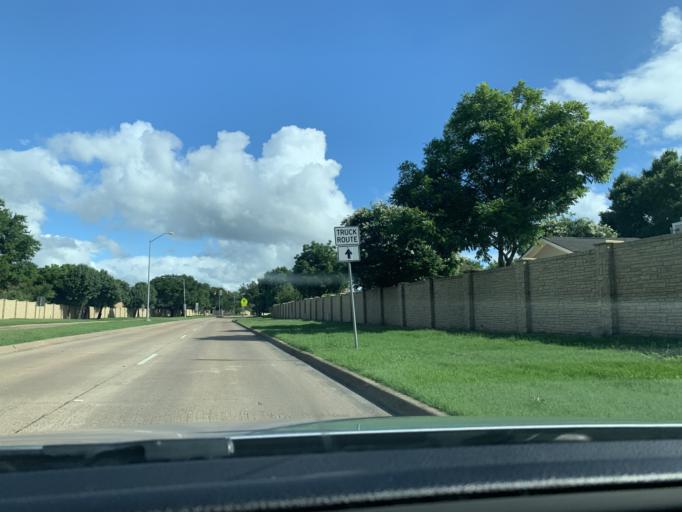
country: US
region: Texas
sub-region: Dallas County
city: Grand Prairie
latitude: 32.6650
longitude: -97.0427
